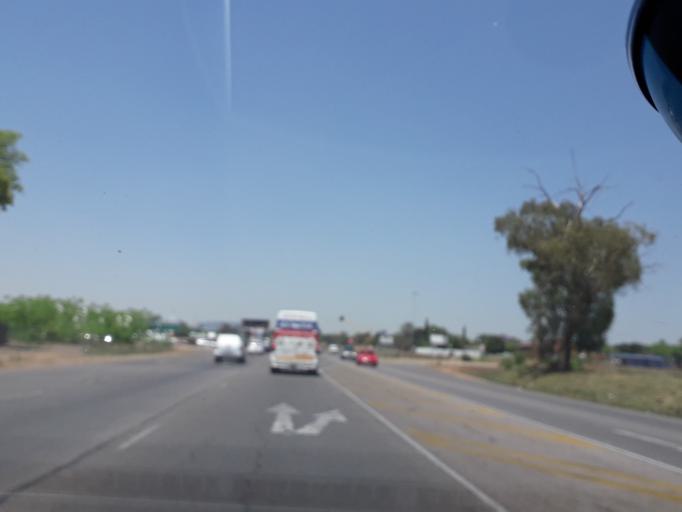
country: ZA
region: Gauteng
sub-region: City of Tshwane Metropolitan Municipality
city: Centurion
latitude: -25.8909
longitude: 28.1604
